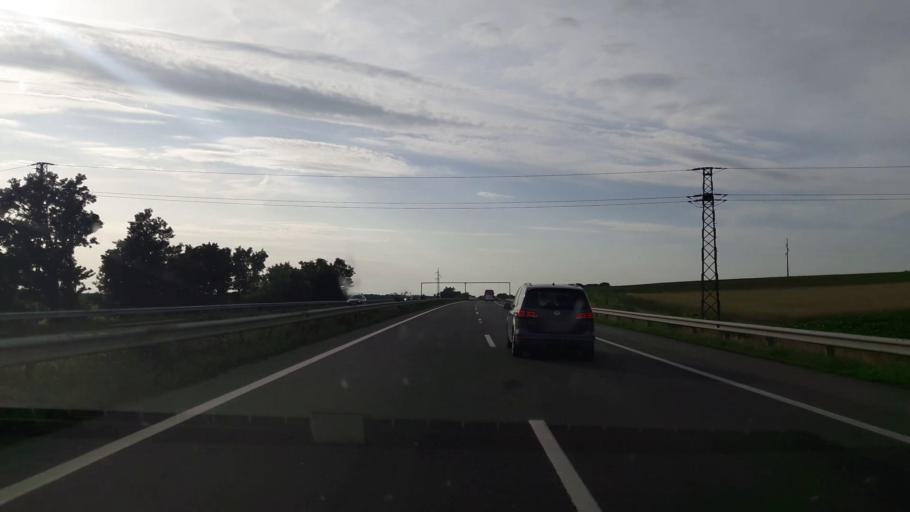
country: AT
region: Burgenland
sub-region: Eisenstadt-Umgebung
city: Steinbrunn
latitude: 47.8413
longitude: 16.4382
